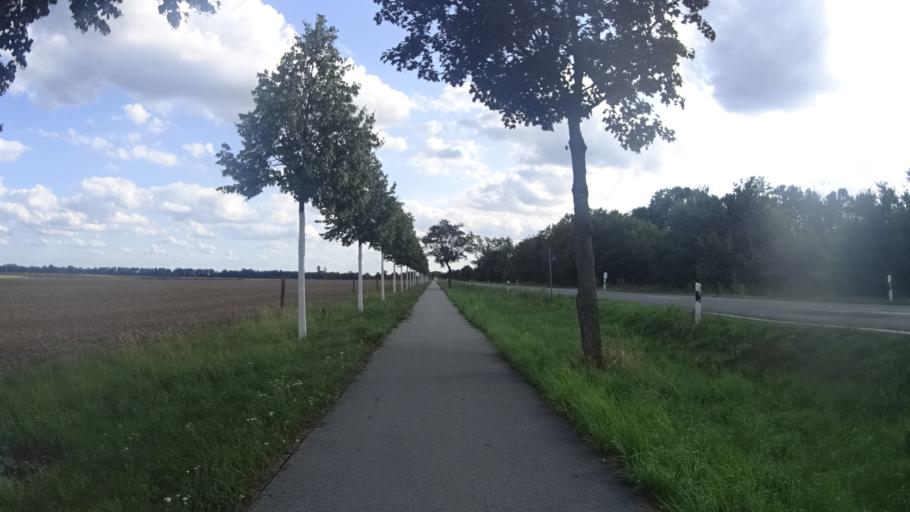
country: DE
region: Brandenburg
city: Rathenow
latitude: 52.6459
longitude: 12.3315
